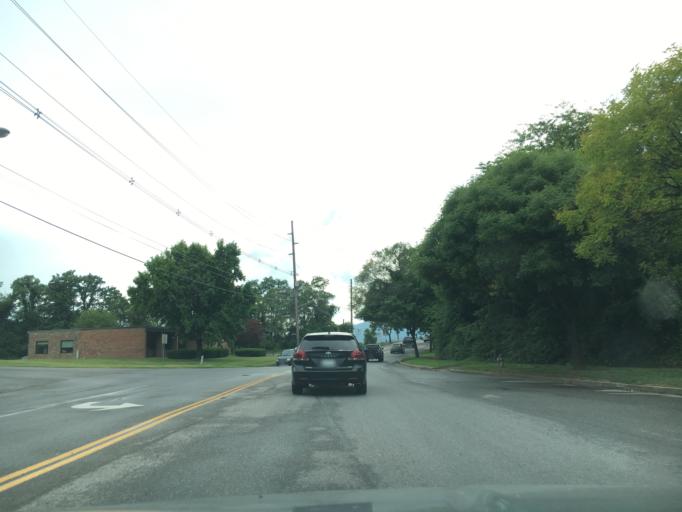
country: US
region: Virginia
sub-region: City of Salem
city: Salem
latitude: 37.2865
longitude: -80.0443
